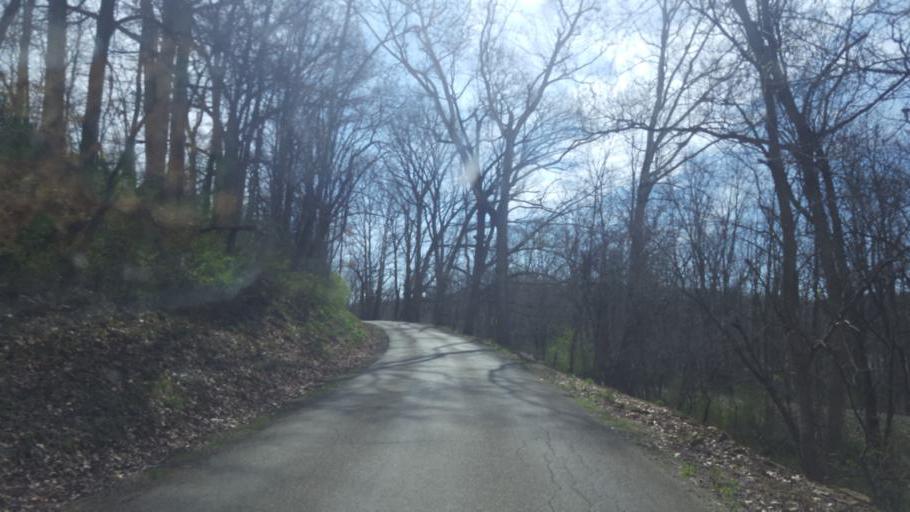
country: US
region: Ohio
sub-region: Knox County
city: Mount Vernon
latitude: 40.3763
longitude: -82.4589
